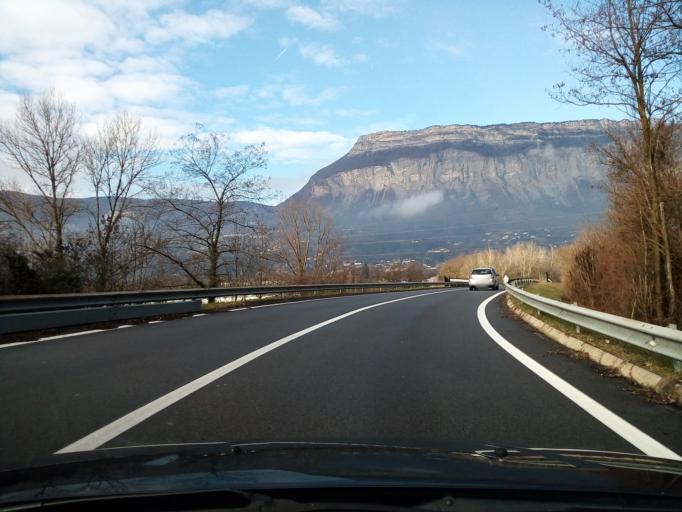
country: FR
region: Rhone-Alpes
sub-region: Departement de l'Isere
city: Meylan
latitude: 45.2053
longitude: 5.7930
